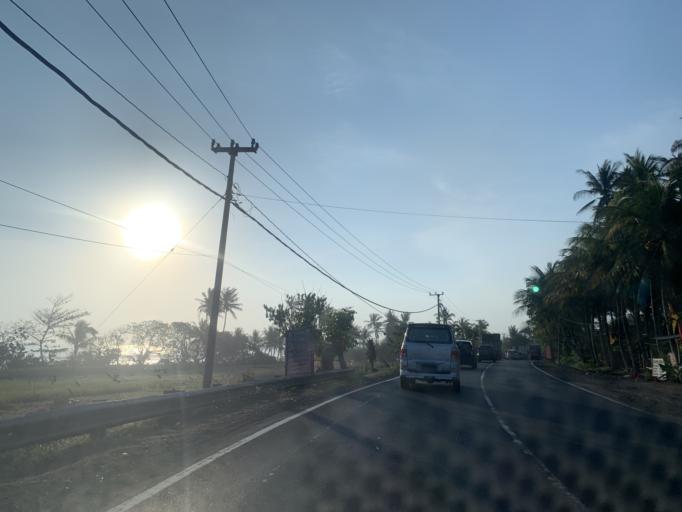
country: ID
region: Bali
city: Angkahgede
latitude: -8.4780
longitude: 114.9370
